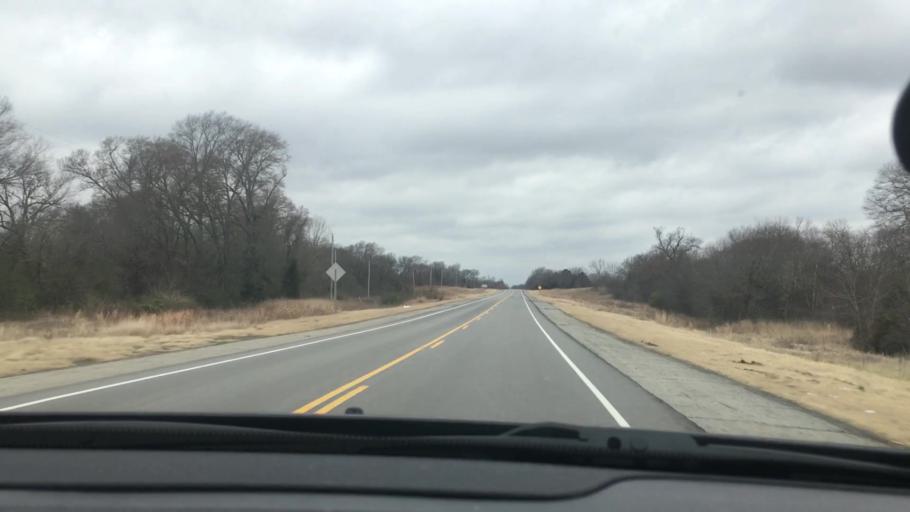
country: US
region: Oklahoma
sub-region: Atoka County
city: Atoka
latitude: 34.3749
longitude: -96.1556
